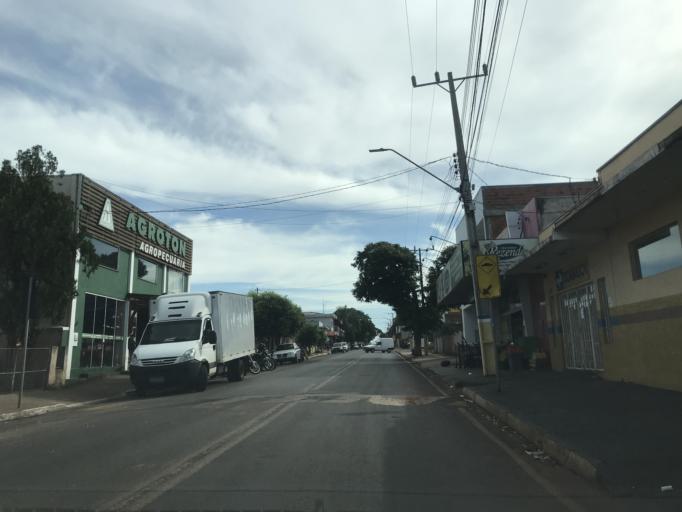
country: BR
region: Parana
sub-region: Paranavai
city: Nova Aurora
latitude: -22.9355
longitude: -52.6868
